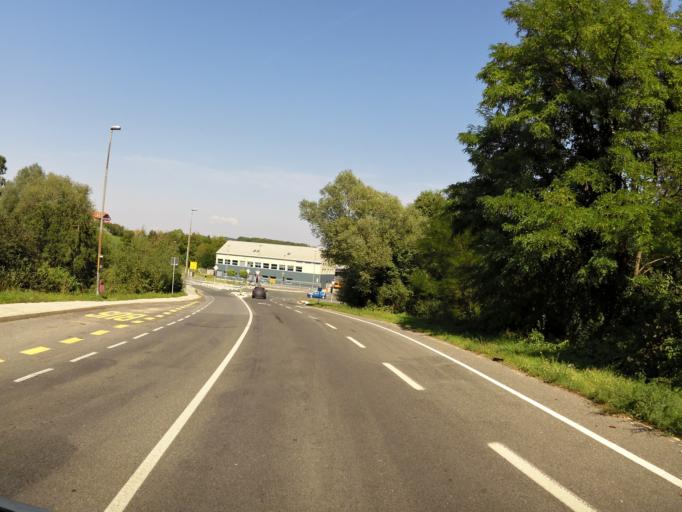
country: SI
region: Pesnica
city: Pesnica pri Mariboru
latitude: 46.5921
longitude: 15.6664
